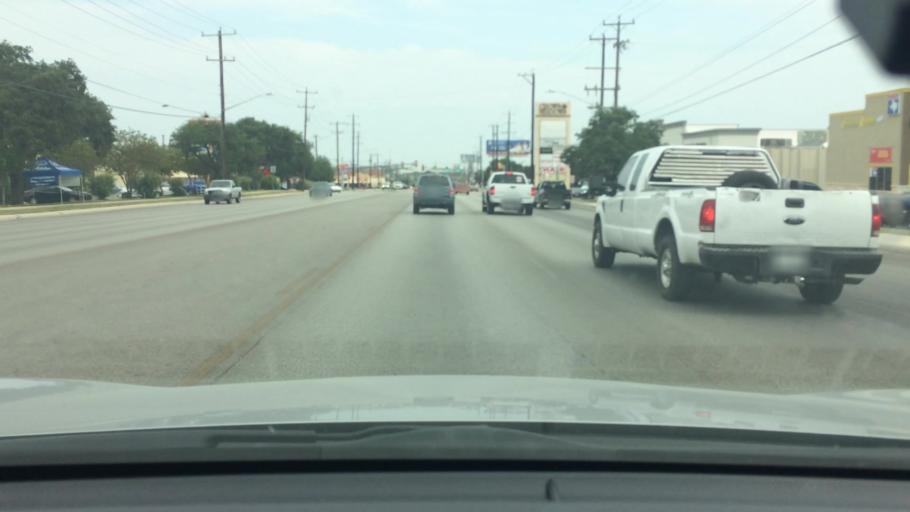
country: US
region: Texas
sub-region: Bexar County
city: Leon Valley
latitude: 29.4606
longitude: -98.6402
